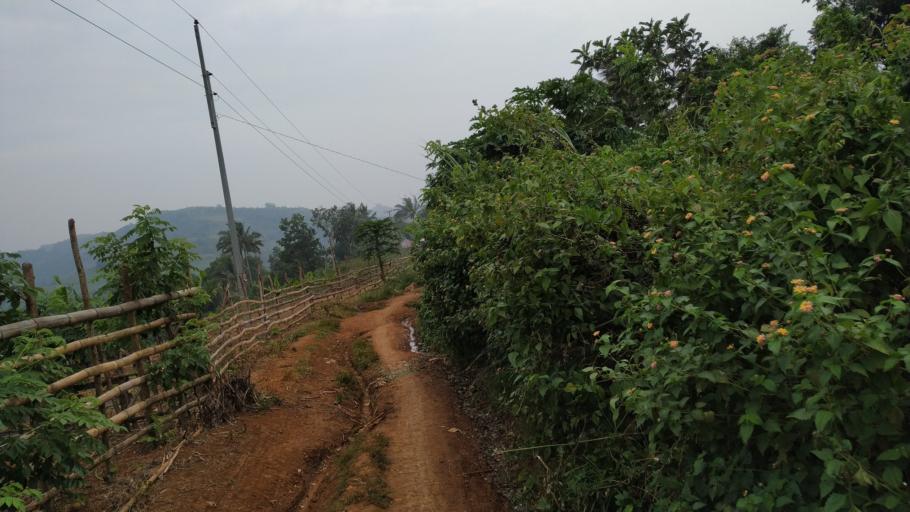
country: PH
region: Western Visayas
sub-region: Province of Negros Occidental
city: Quezon
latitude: 10.4217
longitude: 123.2403
